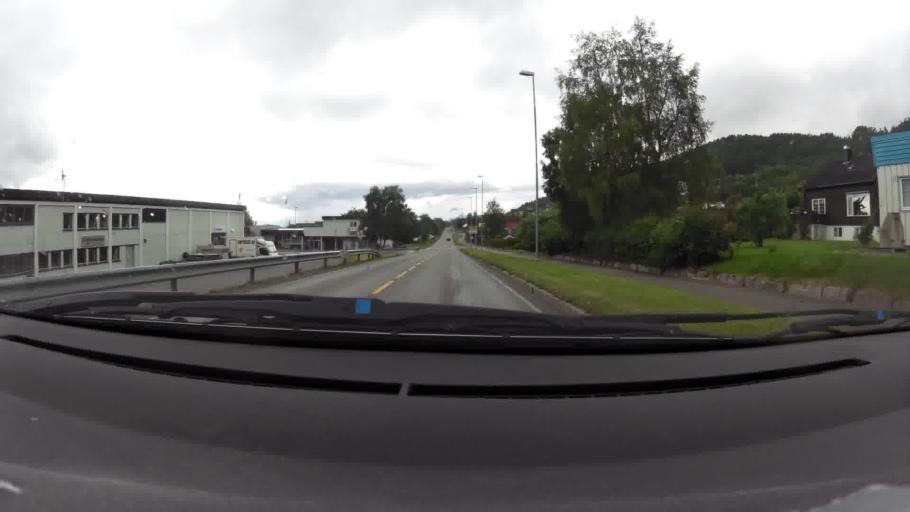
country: NO
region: More og Romsdal
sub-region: Molde
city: Molde
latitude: 62.7470
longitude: 7.2176
